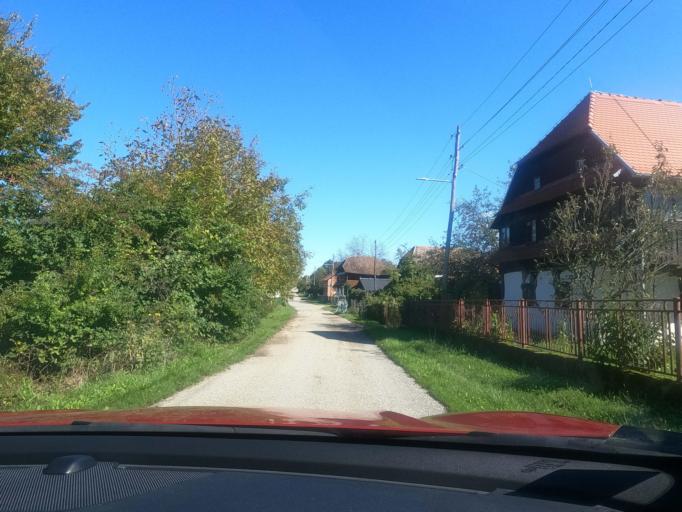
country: HR
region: Sisacko-Moslavacka
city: Petrinja
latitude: 45.3491
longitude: 16.2147
